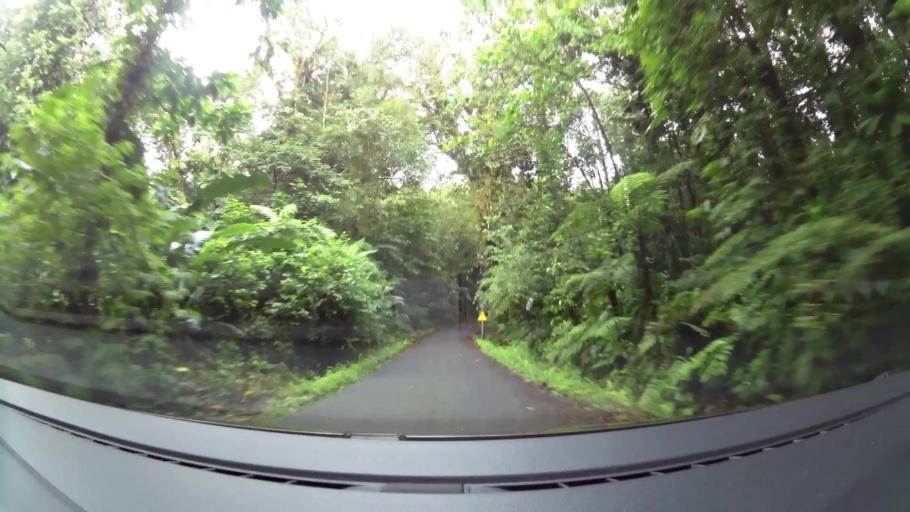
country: GP
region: Guadeloupe
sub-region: Guadeloupe
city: Trois-Rivieres
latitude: 16.0340
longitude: -61.6298
